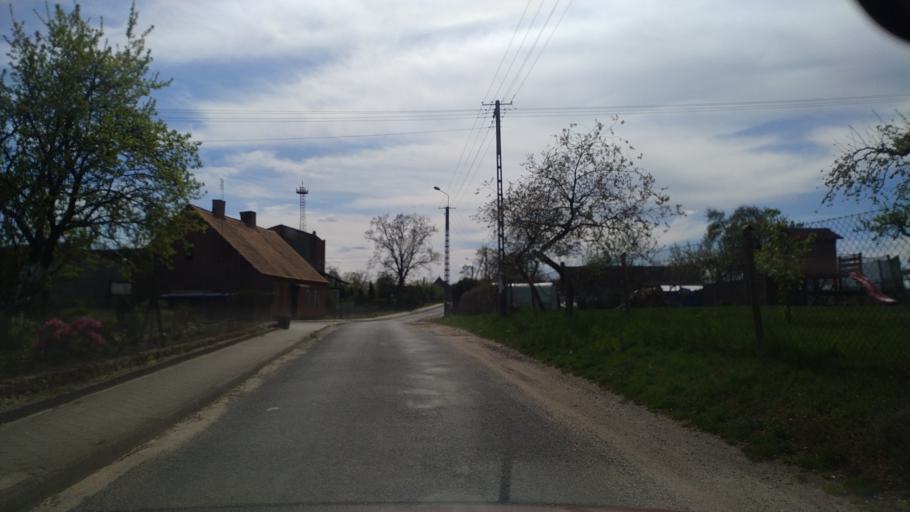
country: PL
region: West Pomeranian Voivodeship
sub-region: Powiat walecki
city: Miroslawiec
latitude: 53.3433
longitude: 16.2495
